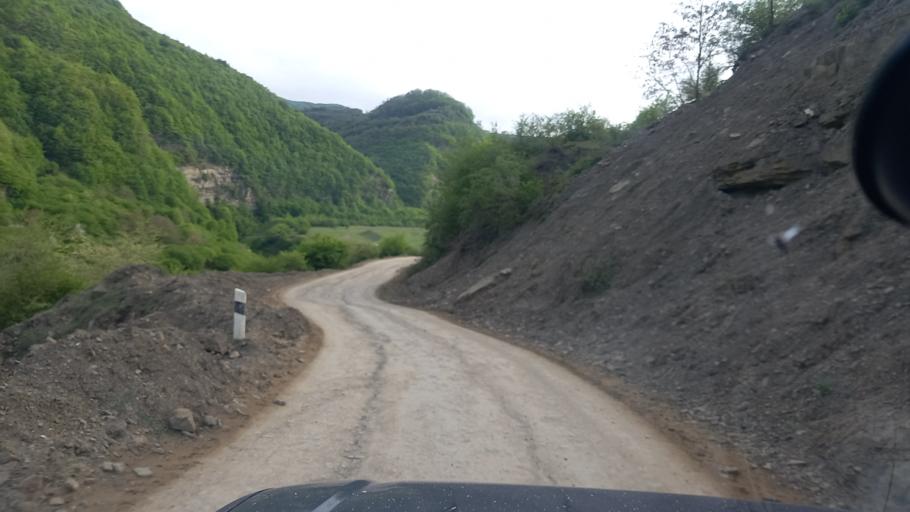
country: RU
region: Dagestan
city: Khuchni
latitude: 41.9661
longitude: 47.8736
